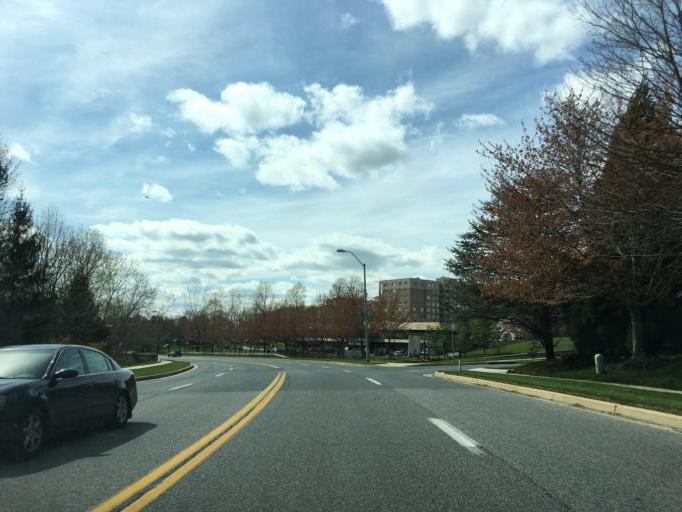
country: US
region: Maryland
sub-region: Baltimore County
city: Mays Chapel
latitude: 39.4581
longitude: -76.6611
